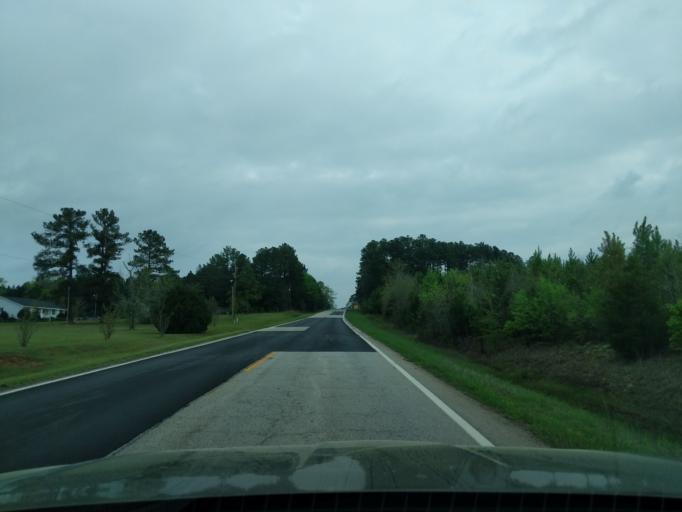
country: US
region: Georgia
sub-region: Lincoln County
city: Lincolnton
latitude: 33.7620
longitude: -82.3776
